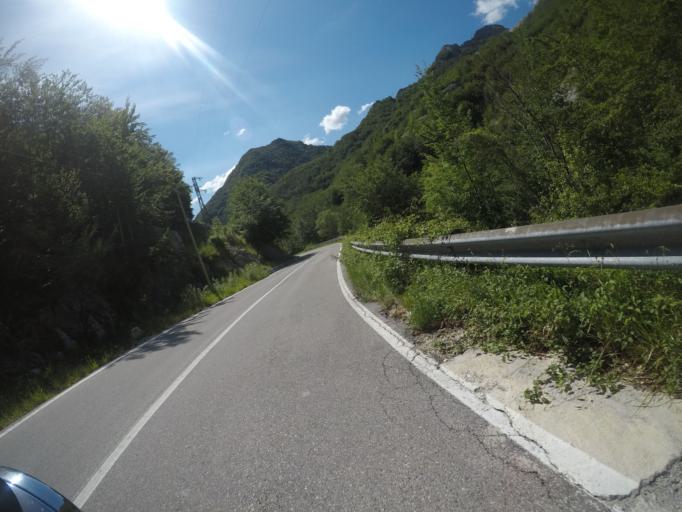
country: IT
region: Tuscany
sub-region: Provincia di Lucca
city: Seravezza
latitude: 44.0596
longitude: 10.2406
